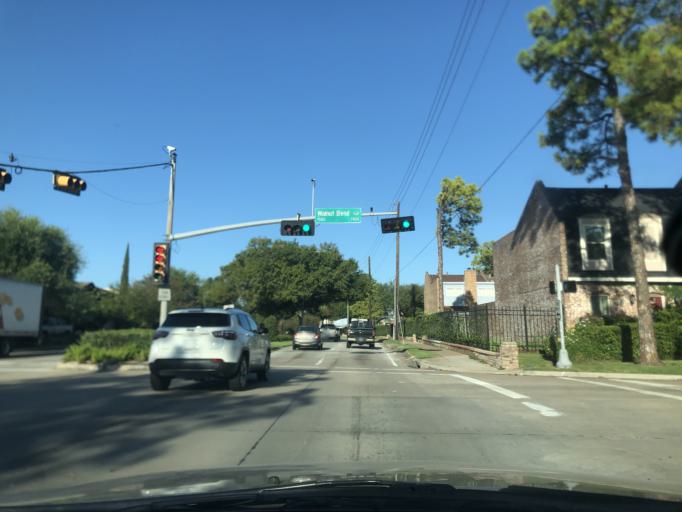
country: US
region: Texas
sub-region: Harris County
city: Bunker Hill Village
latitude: 29.7473
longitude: -95.5649
